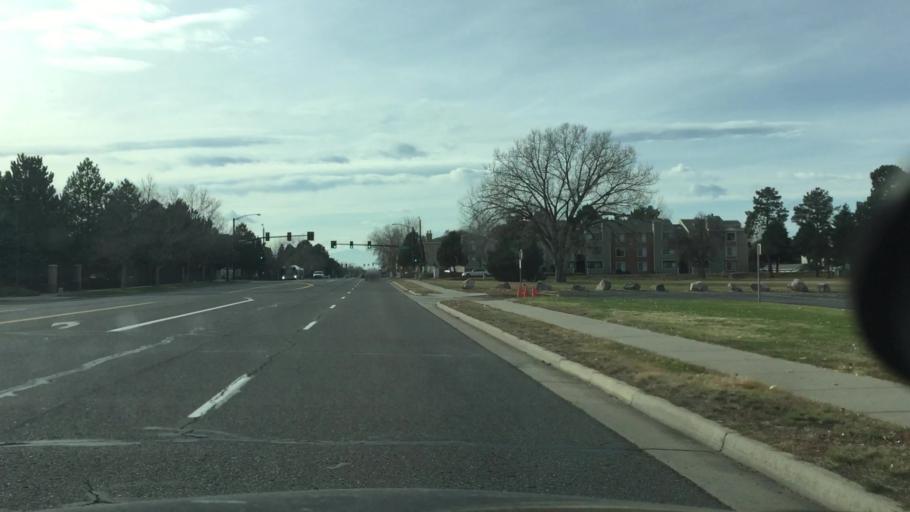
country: US
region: Colorado
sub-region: Arapahoe County
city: Glendale
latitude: 39.6894
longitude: -104.8807
